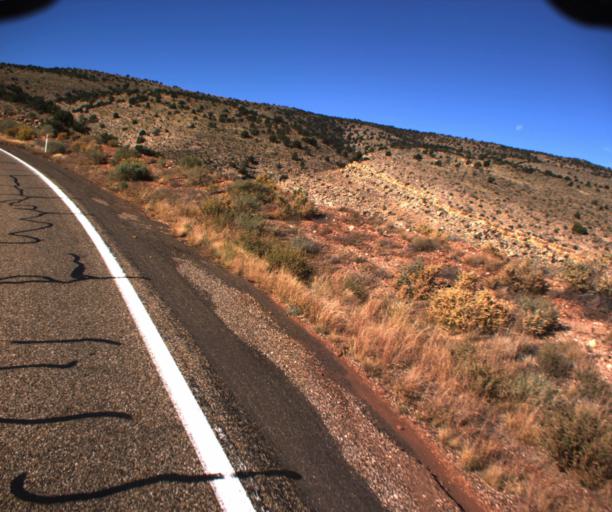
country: US
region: Arizona
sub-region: Coconino County
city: Fredonia
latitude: 36.7312
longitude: -112.0611
